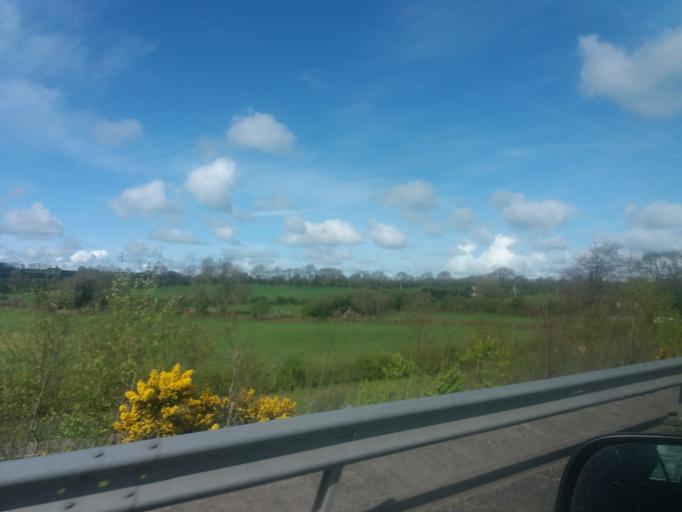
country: IE
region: Ulster
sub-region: An Cabhan
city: Mullagh
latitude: 53.7416
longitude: -6.9716
